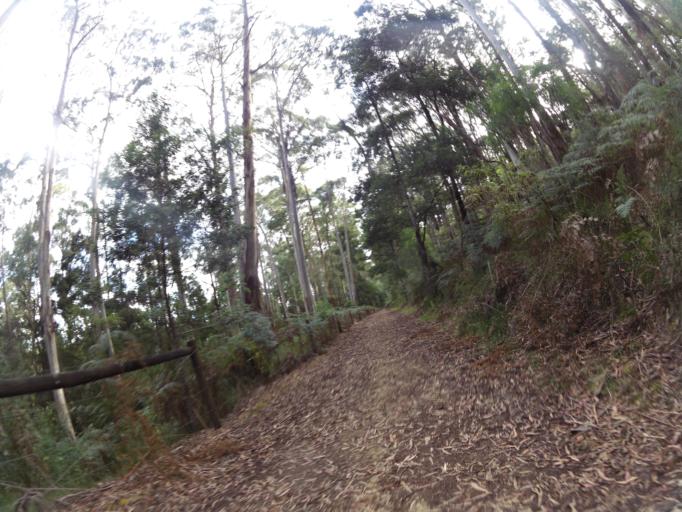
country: AU
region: Victoria
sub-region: Colac-Otway
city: Colac
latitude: -38.4929
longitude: 143.7367
